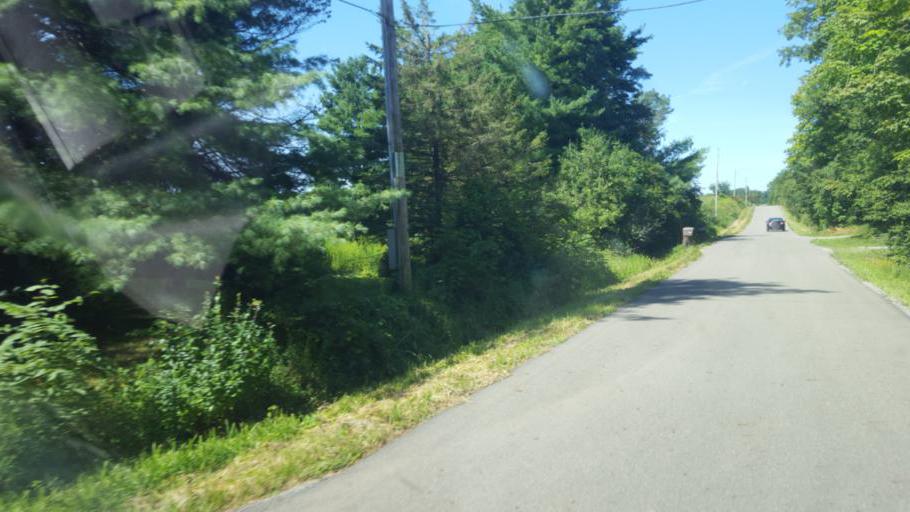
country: US
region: Ohio
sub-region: Morrow County
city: Mount Gilead
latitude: 40.4725
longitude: -82.7136
